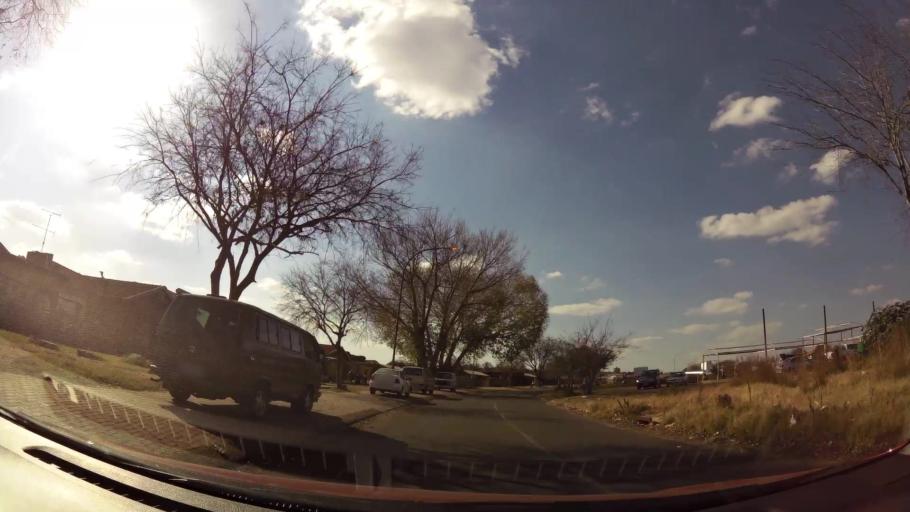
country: ZA
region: Gauteng
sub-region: City of Johannesburg Metropolitan Municipality
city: Roodepoort
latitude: -26.2139
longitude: 27.8839
